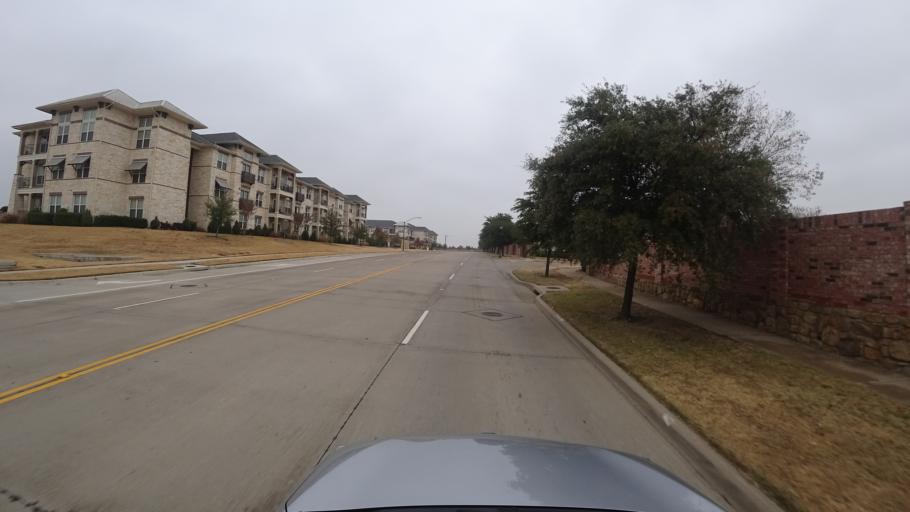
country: US
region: Texas
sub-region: Denton County
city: The Colony
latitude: 33.0624
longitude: -96.9148
